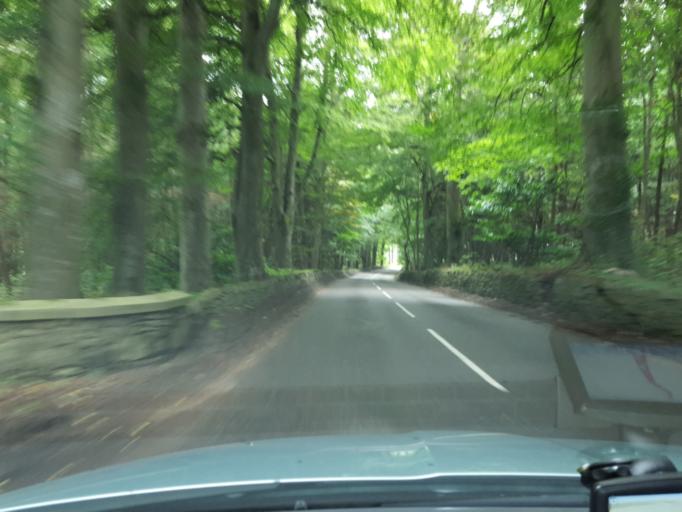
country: GB
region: Scotland
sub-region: Aberdeenshire
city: Kemnay
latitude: 57.1657
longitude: -2.4244
